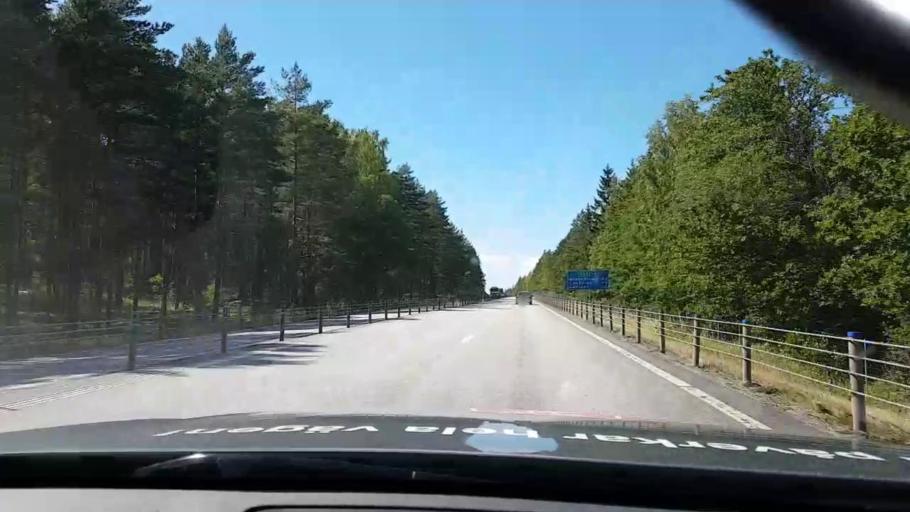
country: SE
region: Kalmar
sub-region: Vasterviks Kommun
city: Gamleby
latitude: 57.8223
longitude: 16.4646
